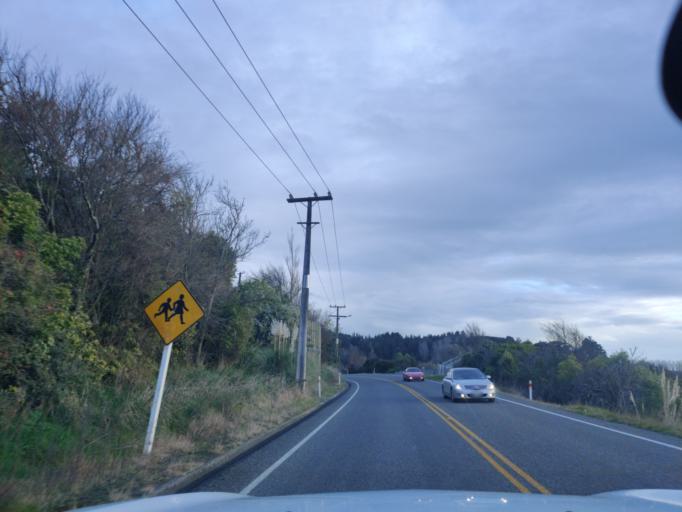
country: NZ
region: Manawatu-Wanganui
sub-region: Palmerston North City
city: Palmerston North
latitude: -40.3731
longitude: 175.6518
